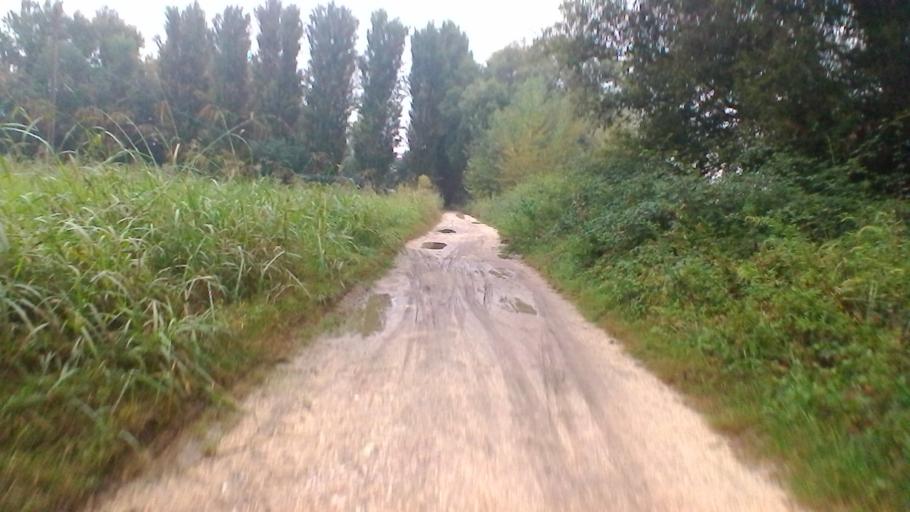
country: IT
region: Veneto
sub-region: Provincia di Verona
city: Montorio
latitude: 45.4262
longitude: 11.0425
